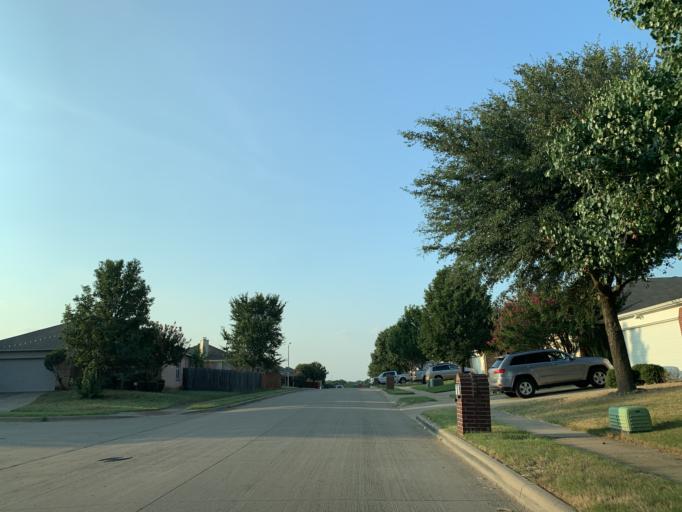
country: US
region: Texas
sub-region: Tarrant County
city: Richland Hills
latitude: 32.7824
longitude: -97.1969
